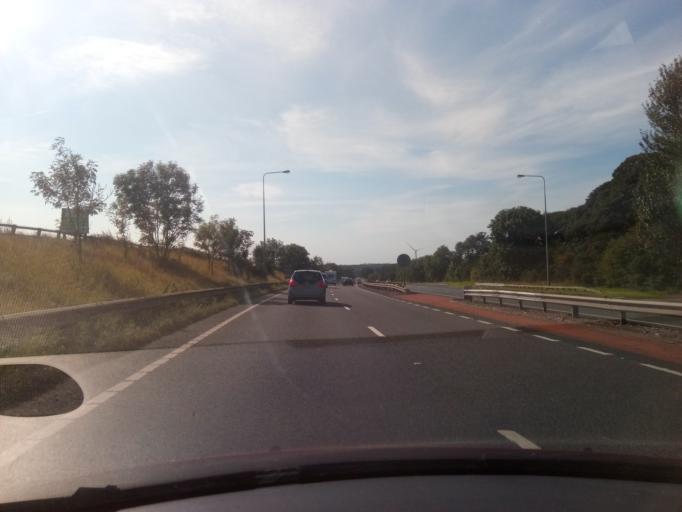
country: GB
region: England
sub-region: Hartlepool
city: Elwick
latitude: 54.6667
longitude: -1.3003
